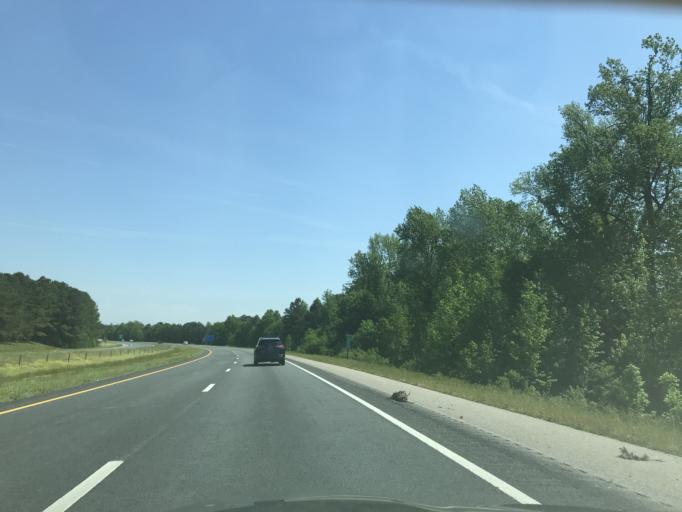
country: US
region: North Carolina
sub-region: Johnston County
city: Benson
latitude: 35.3339
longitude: -78.4593
